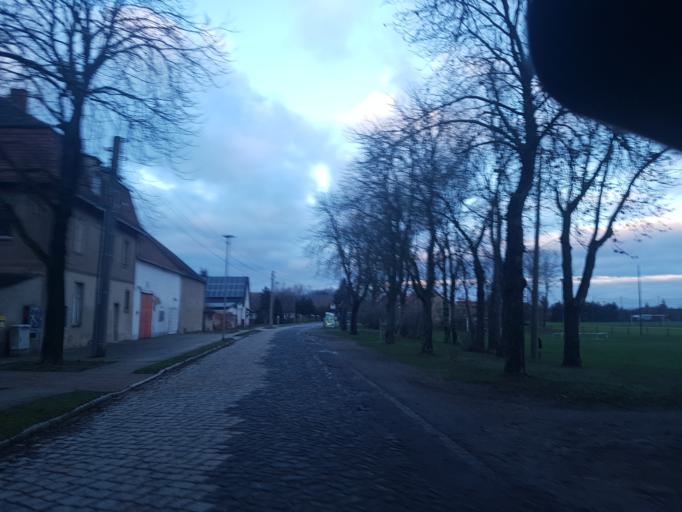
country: DE
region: Brandenburg
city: Muhlberg
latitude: 51.4732
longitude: 13.2043
